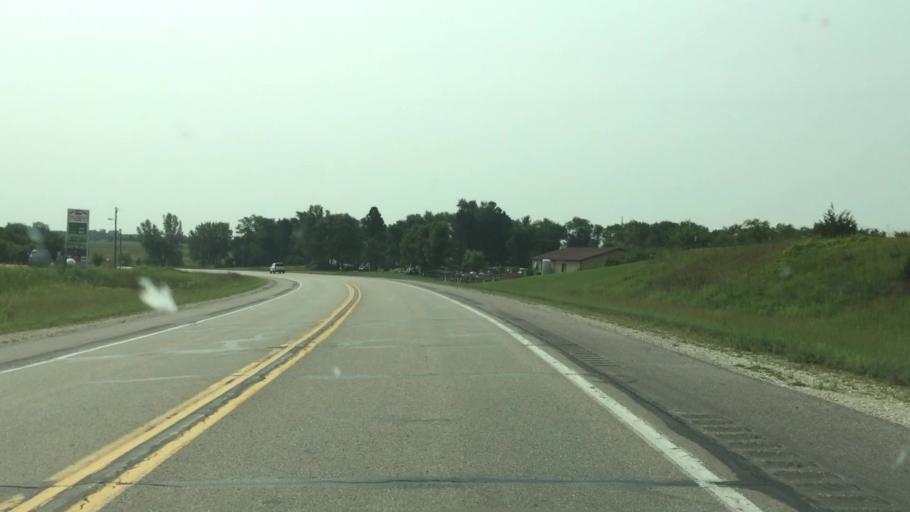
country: US
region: Iowa
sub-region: Dickinson County
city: Milford
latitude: 43.3451
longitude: -95.1792
